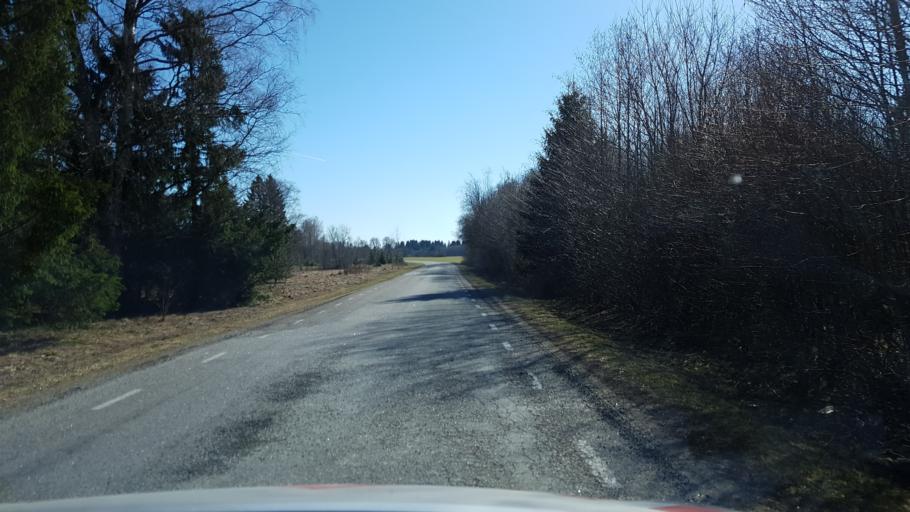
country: EE
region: Laeaene-Virumaa
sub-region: Someru vald
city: Someru
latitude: 59.3872
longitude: 26.4709
